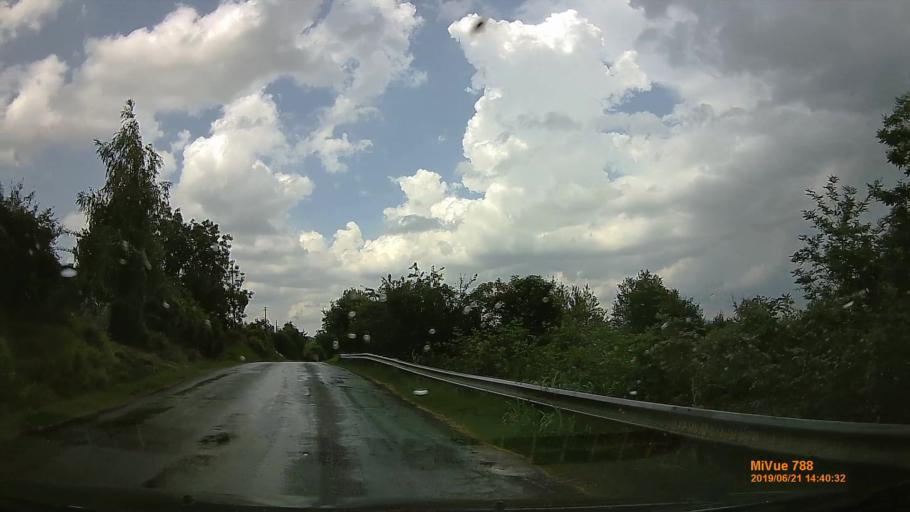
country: HU
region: Baranya
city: Hosszuheteny
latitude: 46.1093
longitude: 18.3137
